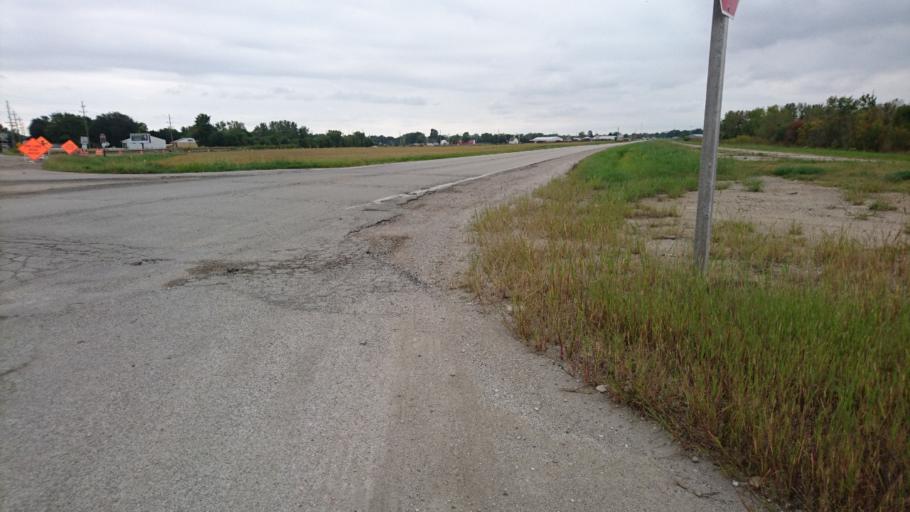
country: US
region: Illinois
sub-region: Livingston County
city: Pontiac
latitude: 40.8987
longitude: -88.6240
